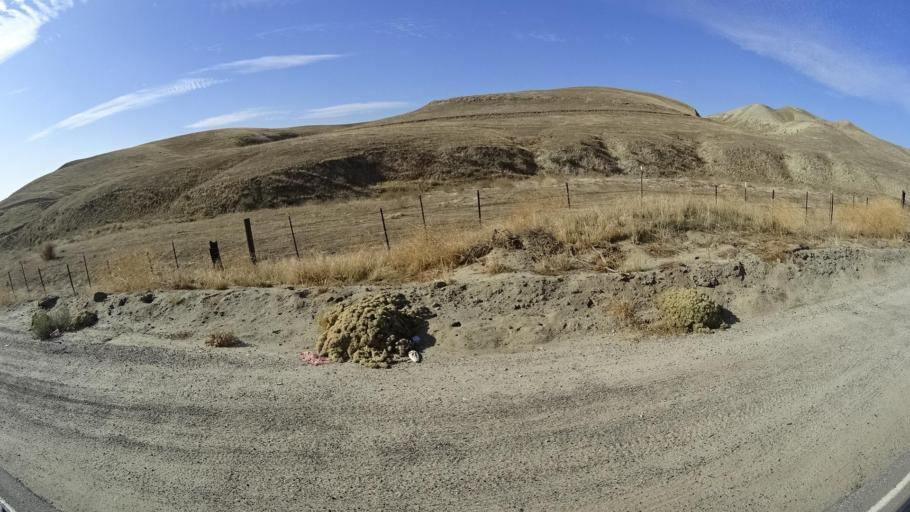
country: US
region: California
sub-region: Kern County
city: Oildale
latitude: 35.5335
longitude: -118.9610
